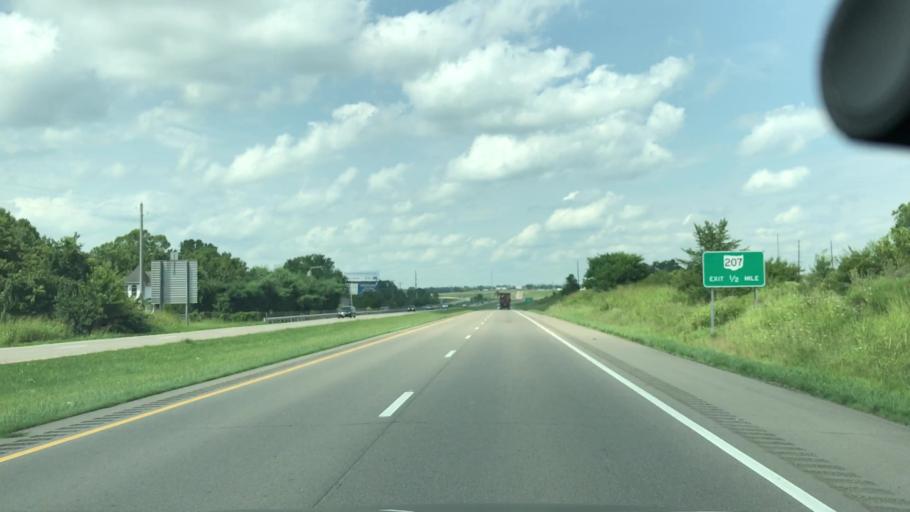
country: US
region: Ohio
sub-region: Ross County
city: Chillicothe
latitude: 39.4038
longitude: -82.9742
